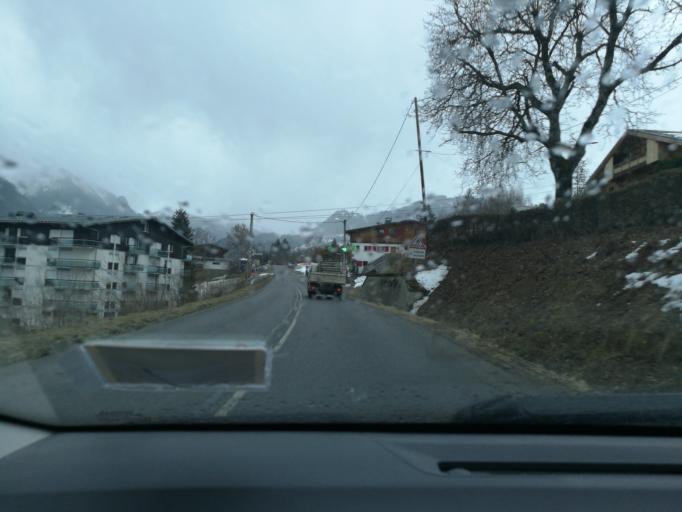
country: FR
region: Rhone-Alpes
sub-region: Departement de la Haute-Savoie
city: Saint-Gervais-les-Bains
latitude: 45.8880
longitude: 6.7020
